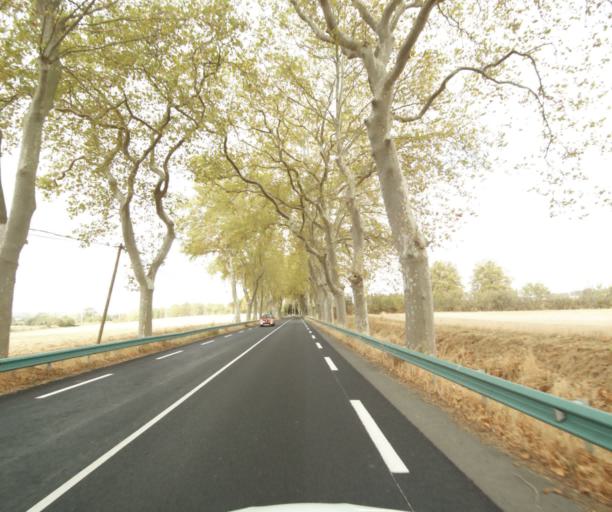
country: FR
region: Midi-Pyrenees
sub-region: Departement de la Haute-Garonne
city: Villefranche-de-Lauragais
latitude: 43.4129
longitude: 1.7023
